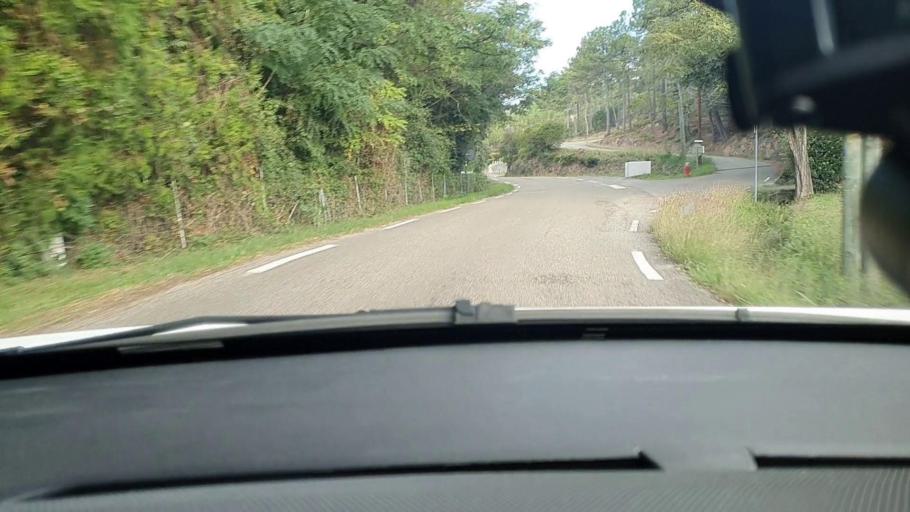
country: FR
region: Languedoc-Roussillon
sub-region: Departement du Gard
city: Besseges
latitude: 44.3050
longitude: 4.0853
